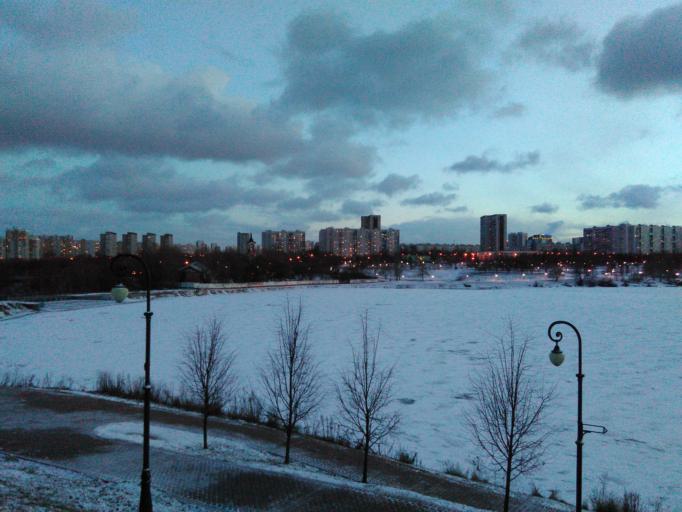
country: RU
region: Moscow
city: Mar'ino
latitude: 55.6333
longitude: 37.7287
